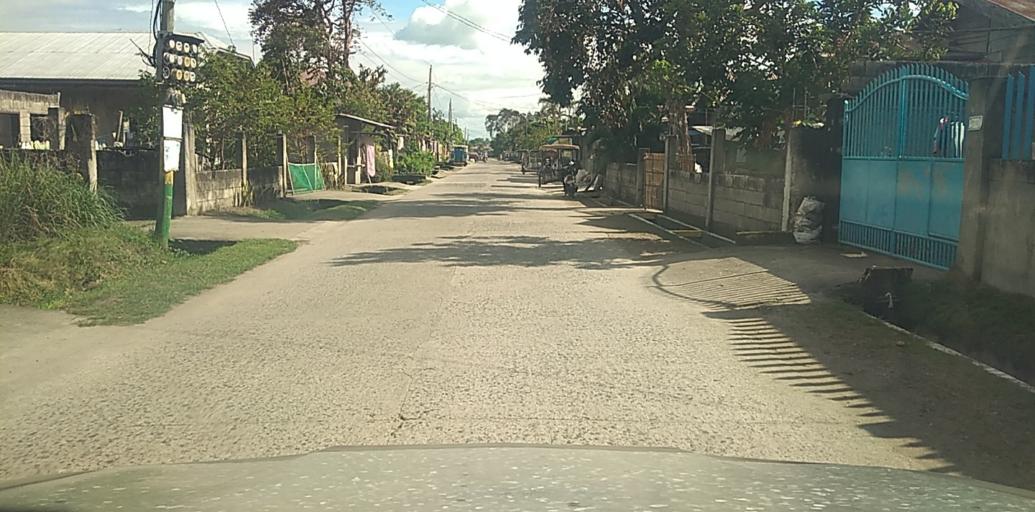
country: PH
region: Central Luzon
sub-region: Province of Pampanga
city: Panlinlang
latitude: 15.1894
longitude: 120.6916
